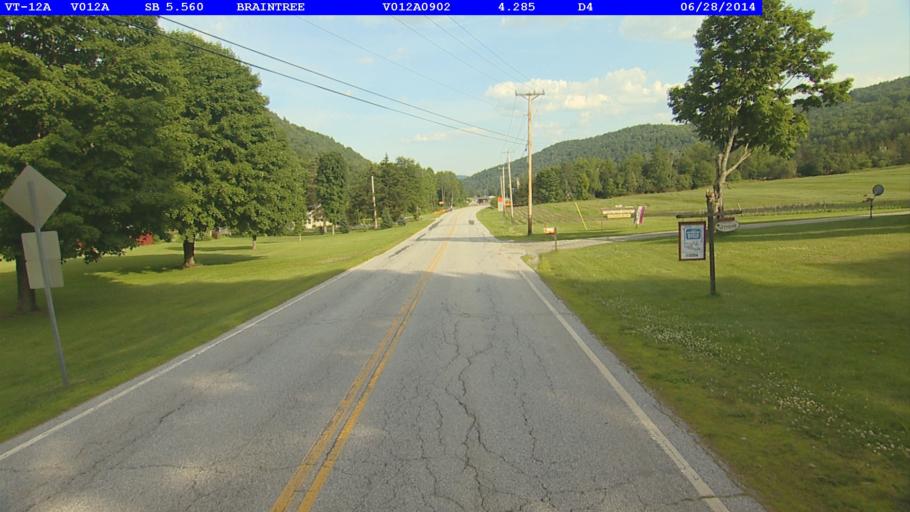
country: US
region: Vermont
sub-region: Orange County
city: Randolph
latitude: 43.9698
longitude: -72.7465
